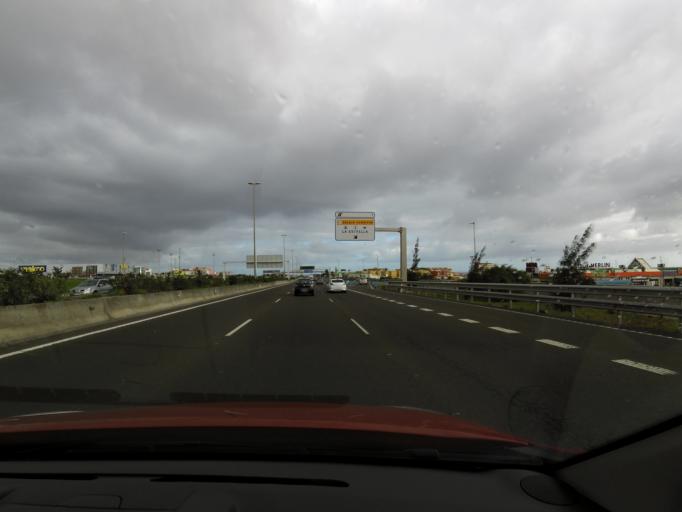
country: ES
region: Canary Islands
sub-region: Provincia de Las Palmas
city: Telde
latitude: 28.0116
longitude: -15.3889
